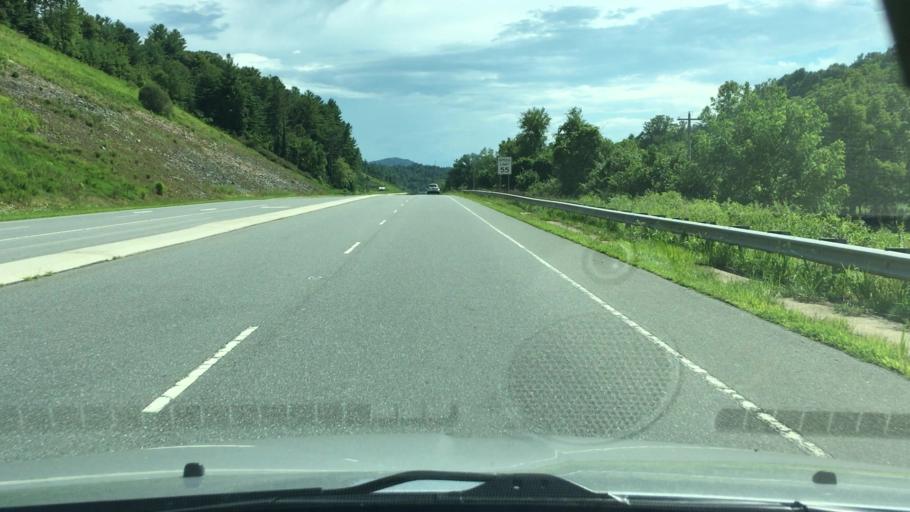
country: US
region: North Carolina
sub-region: Madison County
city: Mars Hill
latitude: 35.8713
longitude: -82.4818
